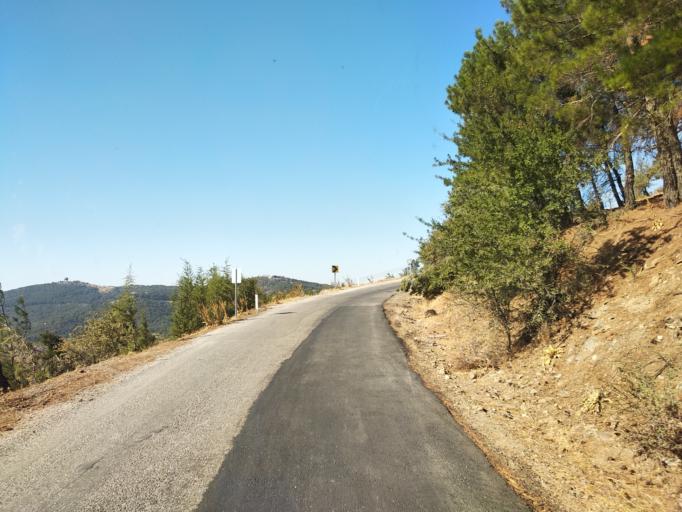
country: TR
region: Izmir
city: Gaziemir
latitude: 38.3095
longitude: 26.9982
